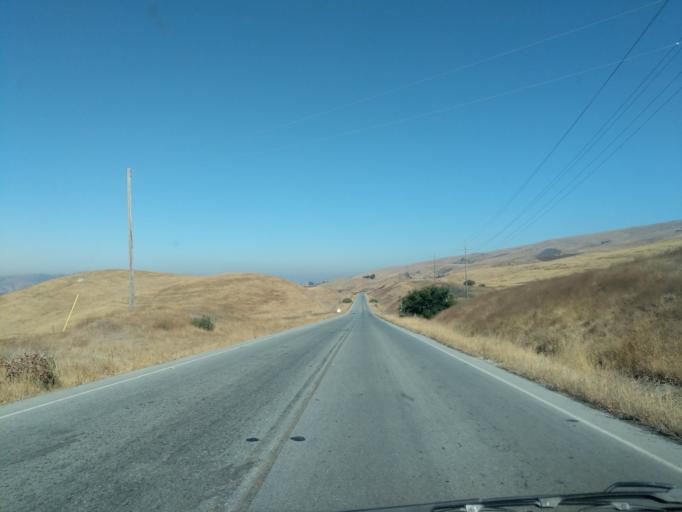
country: US
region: California
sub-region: Santa Clara County
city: Morgan Hill
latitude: 37.1850
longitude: -121.6819
